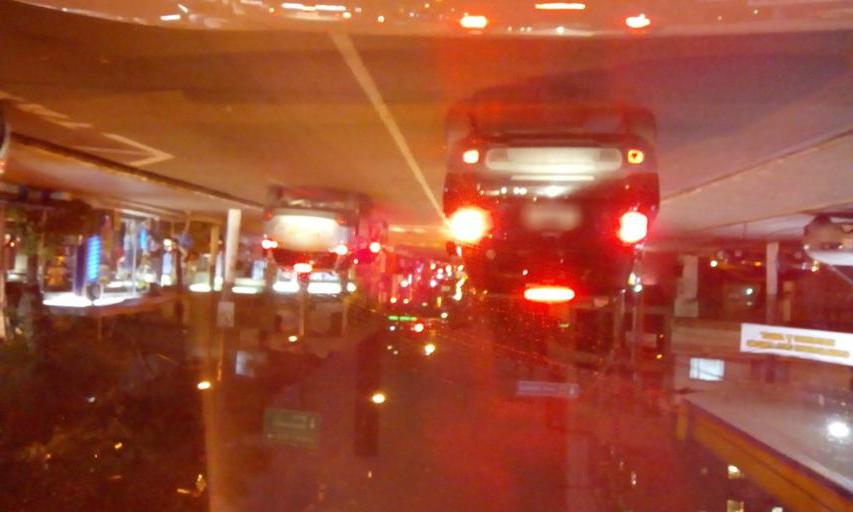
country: BR
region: Sao Paulo
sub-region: Sao Paulo
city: Sao Paulo
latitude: -23.5444
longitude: -46.5856
